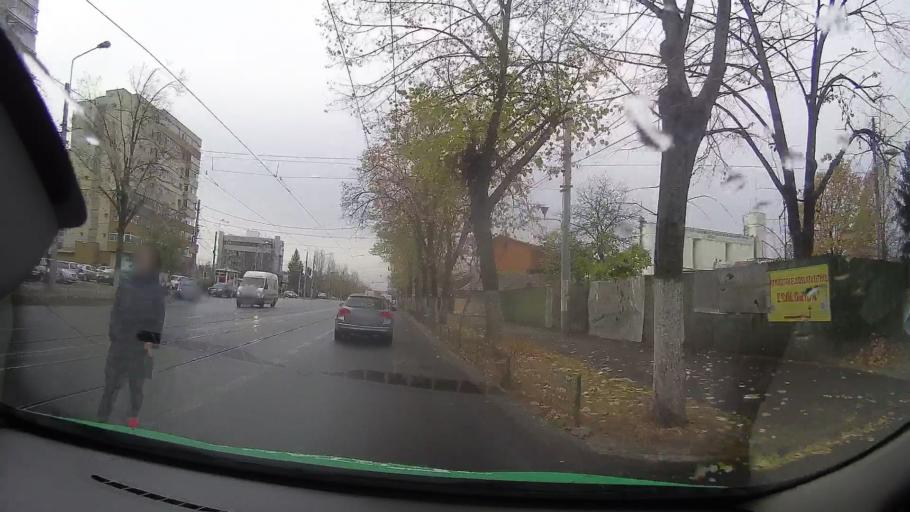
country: RO
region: Prahova
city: Ploiesti
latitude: 44.9442
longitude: 25.9929
